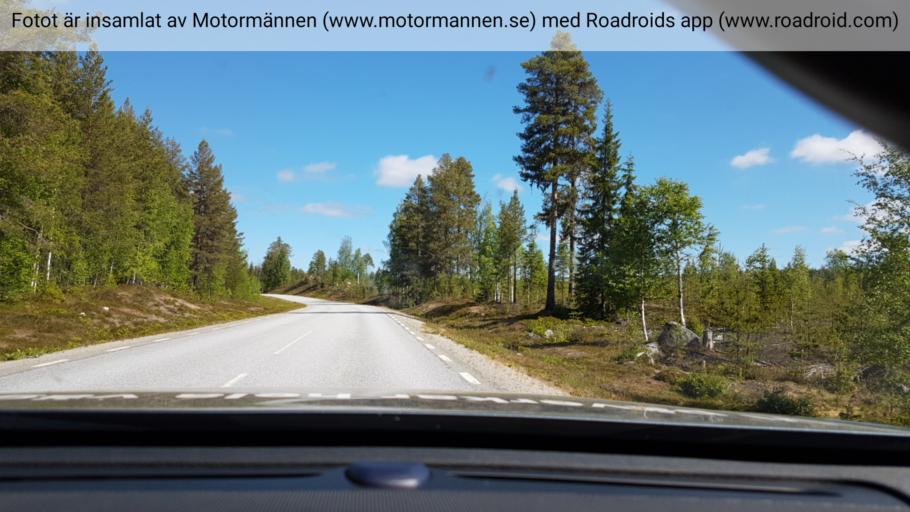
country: SE
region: Vaesterbotten
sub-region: Asele Kommun
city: Asele
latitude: 64.2640
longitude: 17.2731
